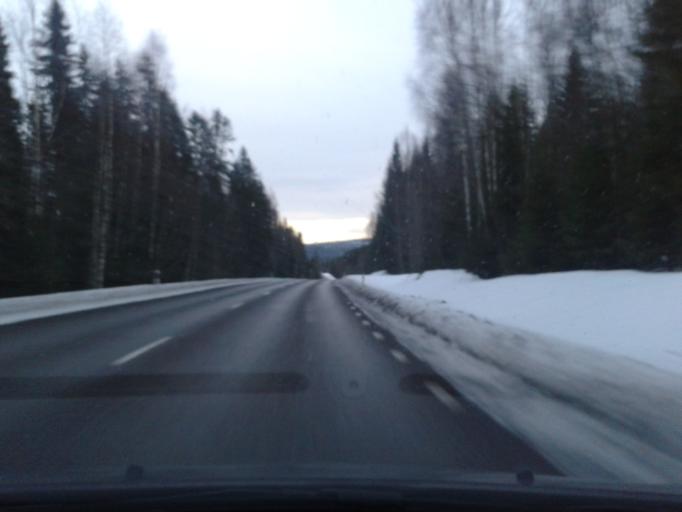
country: SE
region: Vaesternorrland
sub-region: Kramfors Kommun
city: Bollstabruk
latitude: 63.0930
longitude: 17.5274
